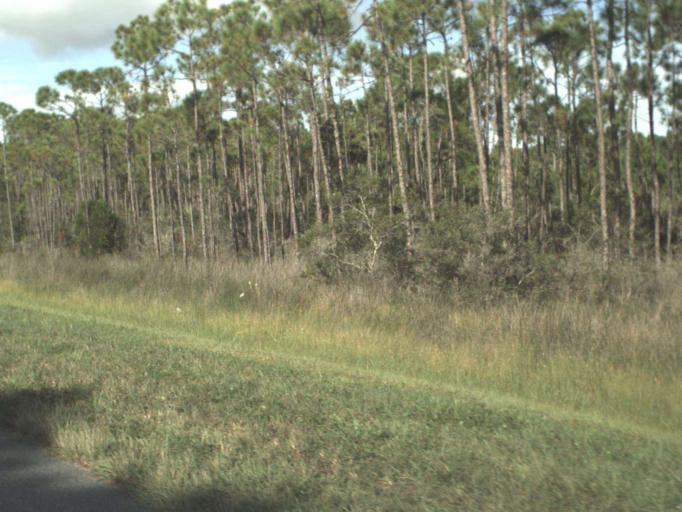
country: US
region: Florida
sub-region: Gulf County
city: Port Saint Joe
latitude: 29.7847
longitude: -85.3011
